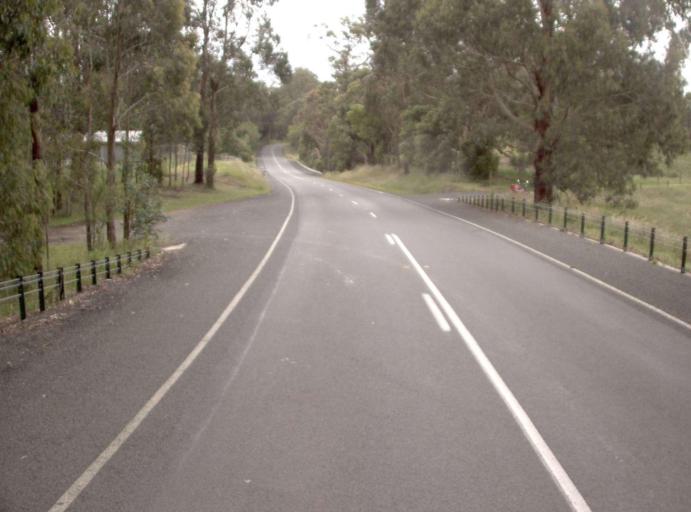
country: AU
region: Victoria
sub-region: Baw Baw
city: Warragul
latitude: -38.0582
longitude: 145.9668
